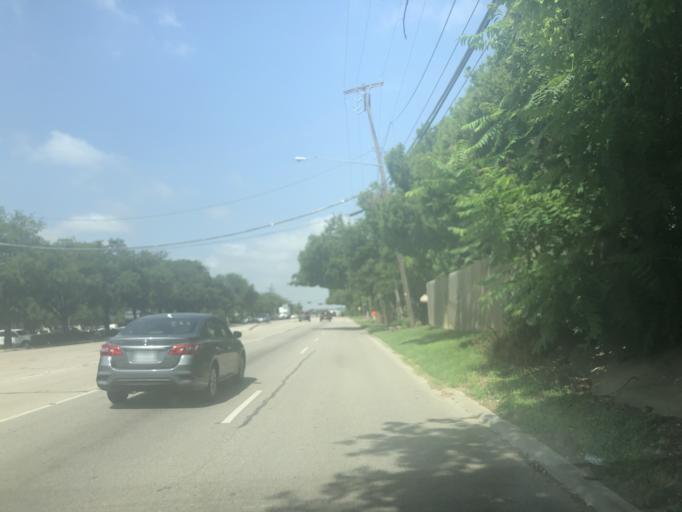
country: US
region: Texas
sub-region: Dallas County
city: University Park
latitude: 32.8628
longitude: -96.8490
